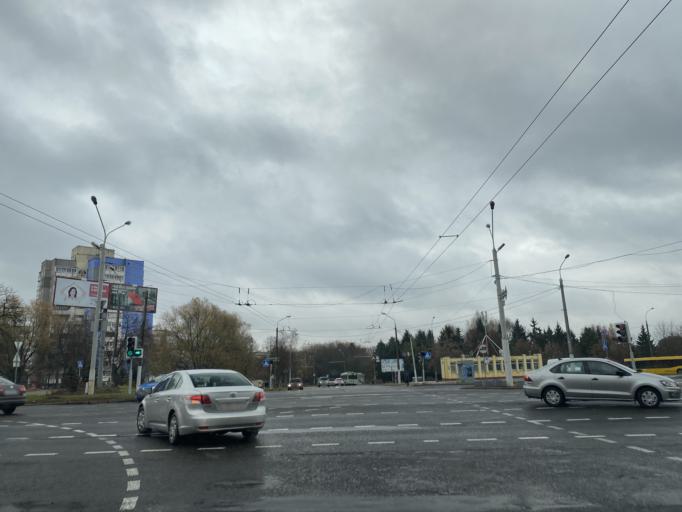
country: BY
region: Minsk
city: Borovlyany
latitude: 53.9559
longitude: 27.6211
